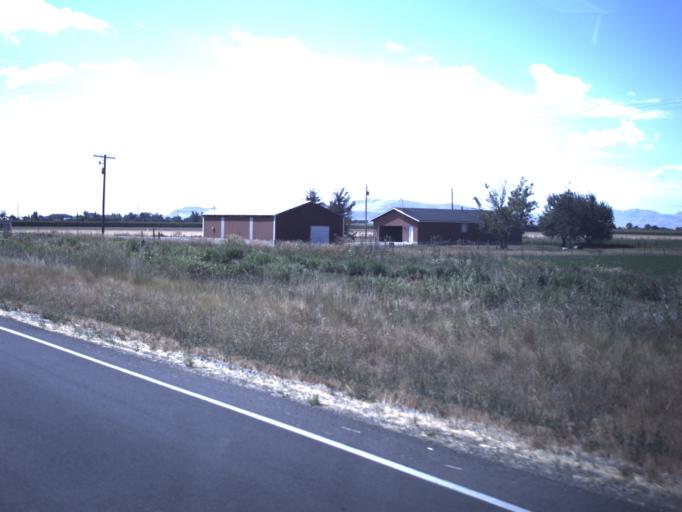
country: US
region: Utah
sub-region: Box Elder County
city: Elwood
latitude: 41.6988
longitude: -112.1419
